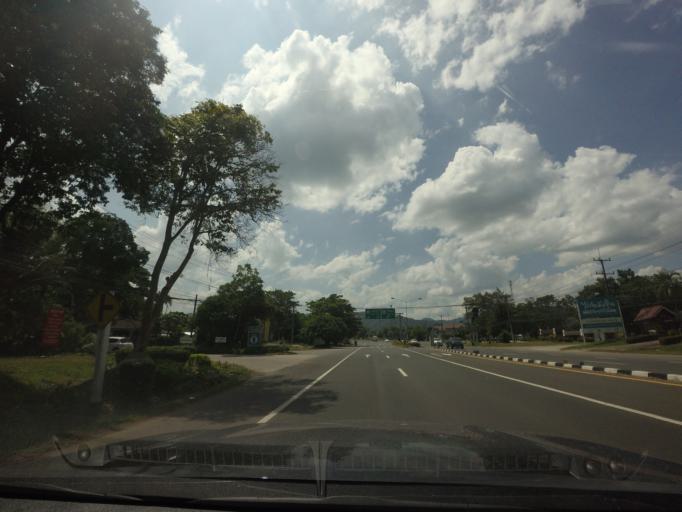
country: TH
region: Phetchabun
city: Phetchabun
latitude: 16.2656
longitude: 101.0499
